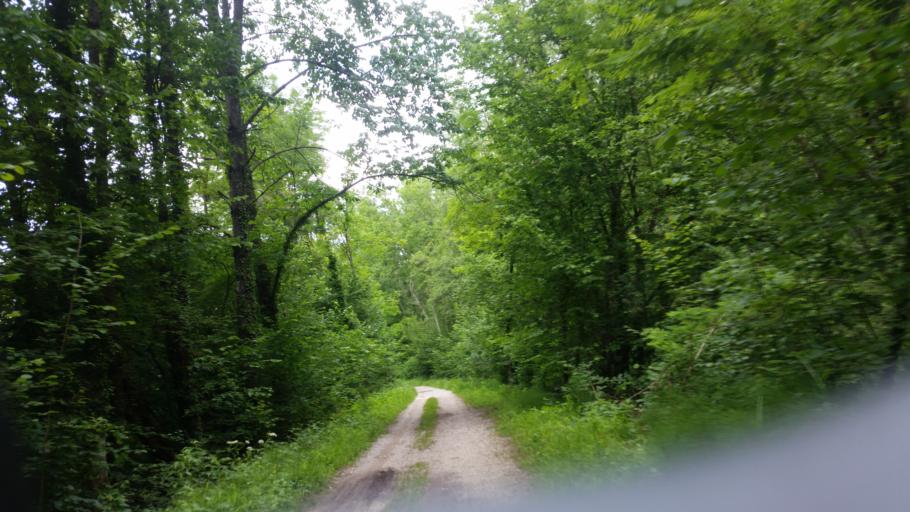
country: CH
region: Fribourg
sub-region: Broye District
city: Estavayer-le-Lac
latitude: 46.8320
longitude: 6.8098
